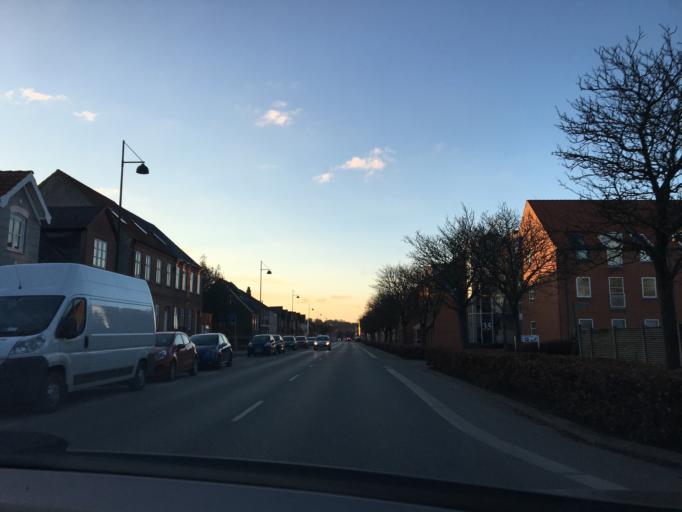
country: DK
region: South Denmark
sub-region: Middelfart Kommune
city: Middelfart
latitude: 55.5022
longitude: 9.7455
